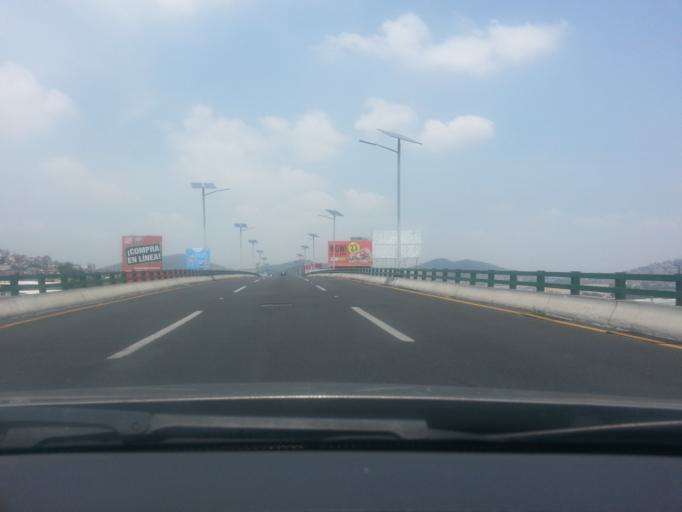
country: MX
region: Mexico
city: Tlalnepantla
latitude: 19.5580
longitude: -99.2061
